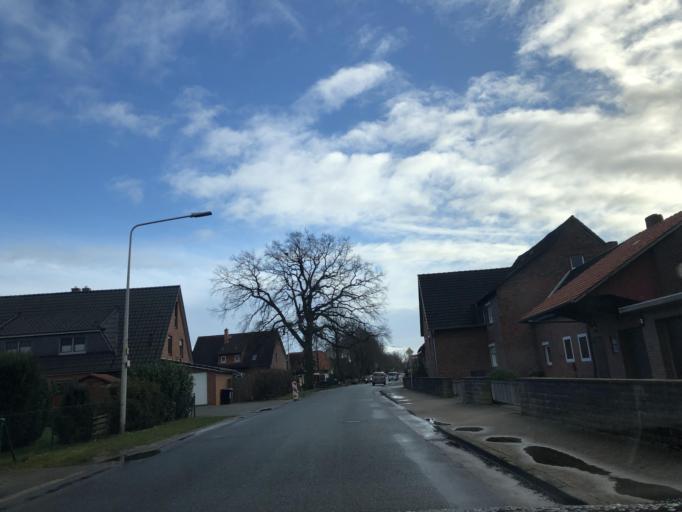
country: DE
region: Lower Saxony
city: Hohnhorst
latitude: 52.3952
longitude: 9.3517
